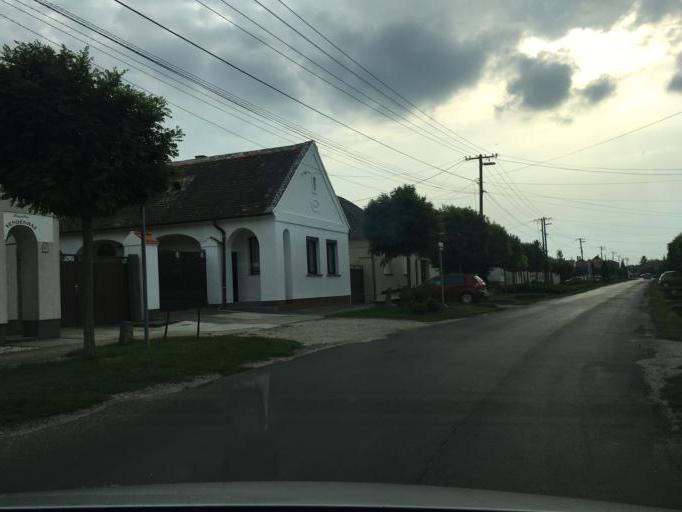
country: HU
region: Gyor-Moson-Sopron
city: Fertod
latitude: 47.6355
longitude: 16.8640
